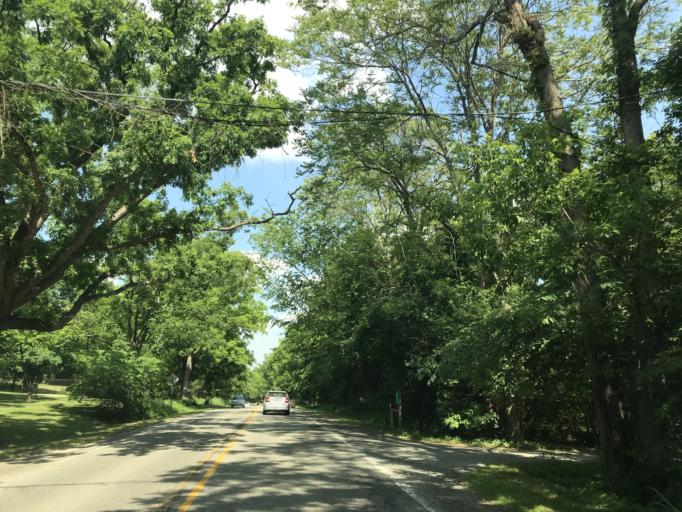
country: US
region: Michigan
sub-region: Washtenaw County
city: Ypsilanti
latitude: 42.2788
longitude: -83.6513
